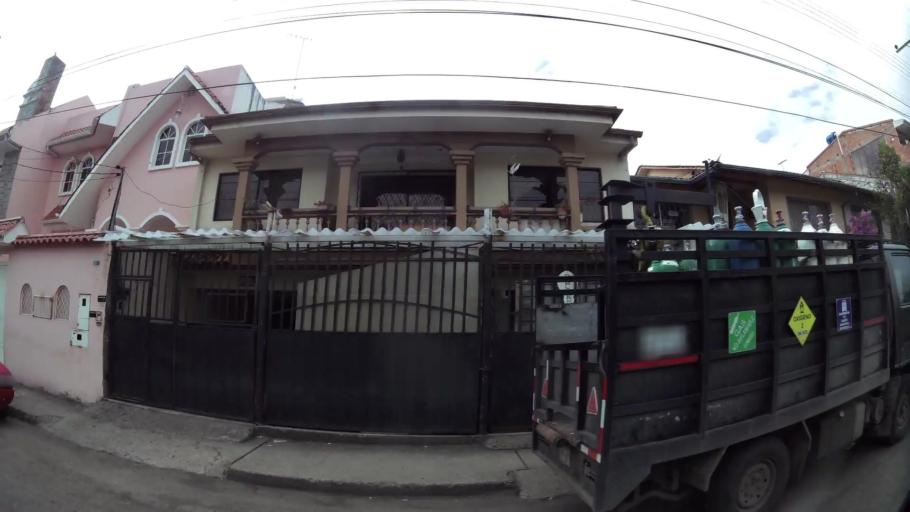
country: EC
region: Azuay
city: Cuenca
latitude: -2.8949
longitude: -78.9831
